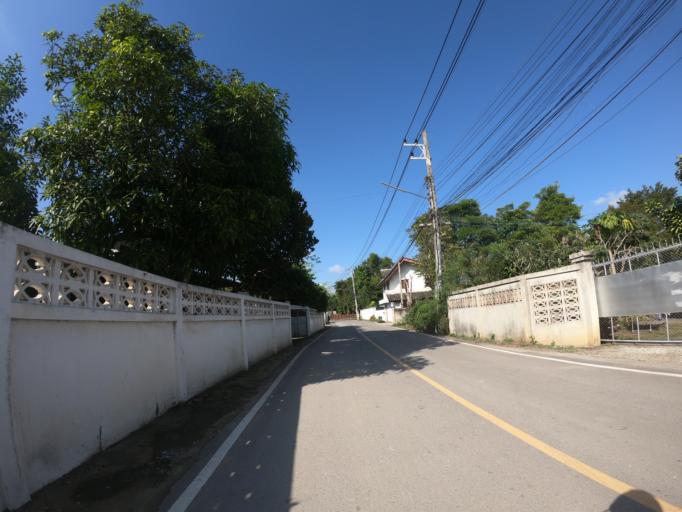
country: TH
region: Chiang Mai
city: Saraphi
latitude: 18.7122
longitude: 99.0052
